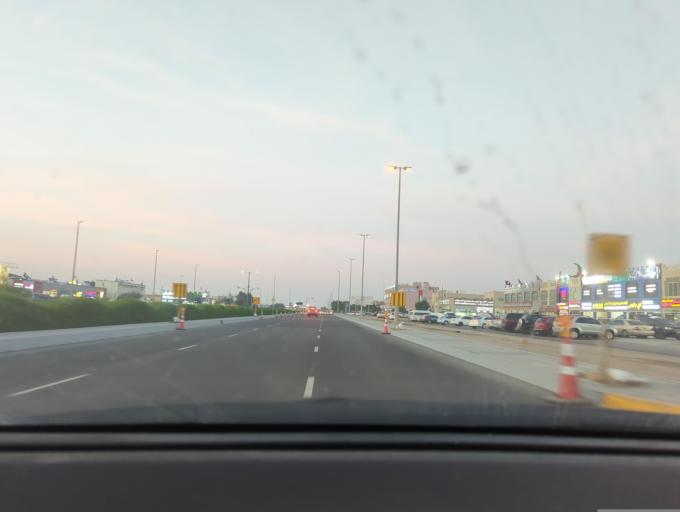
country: AE
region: Abu Dhabi
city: Abu Dhabi
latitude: 24.3756
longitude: 54.5160
